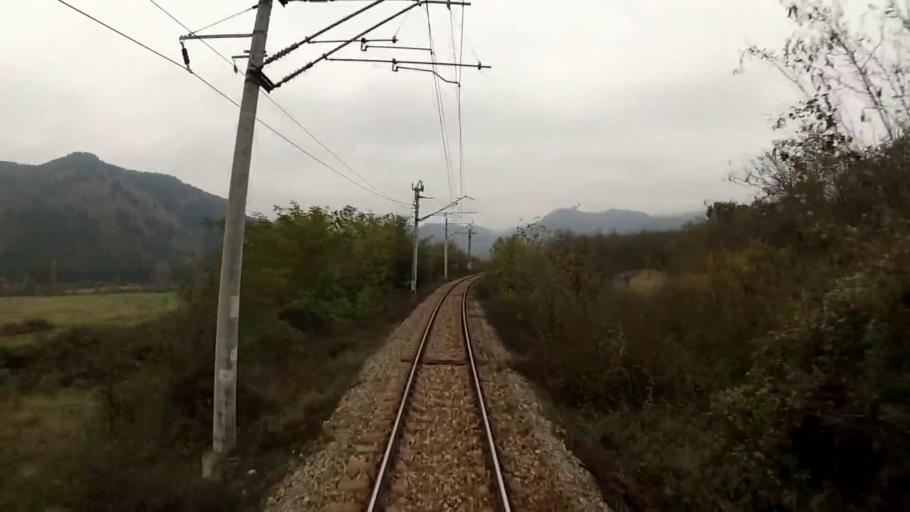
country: RS
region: Central Serbia
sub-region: Pirotski Okrug
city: Dimitrovgrad
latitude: 42.9883
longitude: 22.8515
